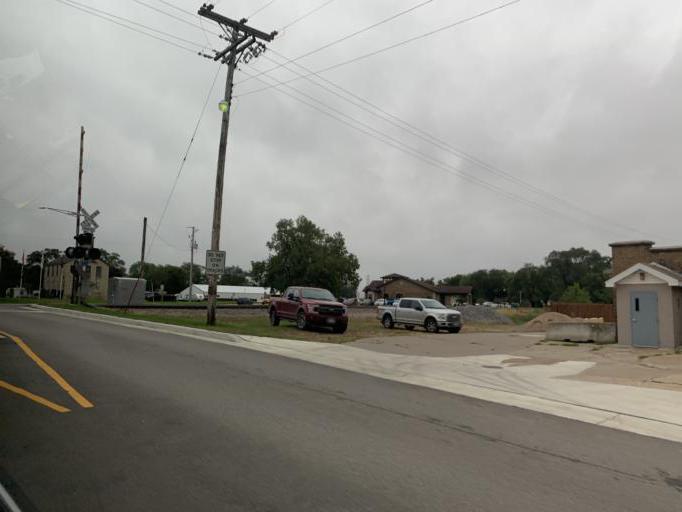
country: US
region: Wisconsin
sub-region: Crawford County
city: Prairie du Chien
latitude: 43.0351
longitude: -91.1387
